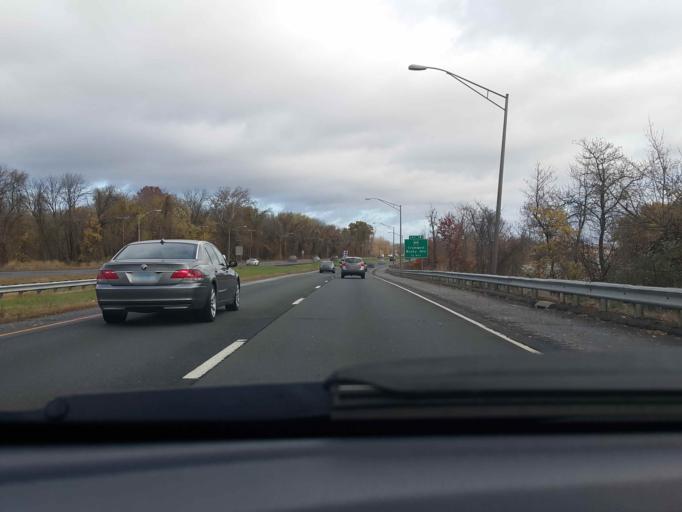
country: US
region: Connecticut
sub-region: Middlesex County
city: Portland
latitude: 41.5751
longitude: -72.6516
